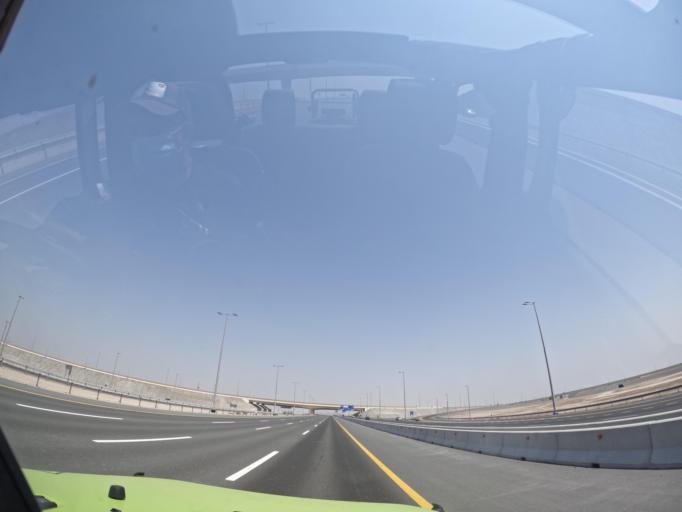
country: AE
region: Abu Dhabi
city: Abu Dhabi
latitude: 24.2866
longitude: 54.5496
